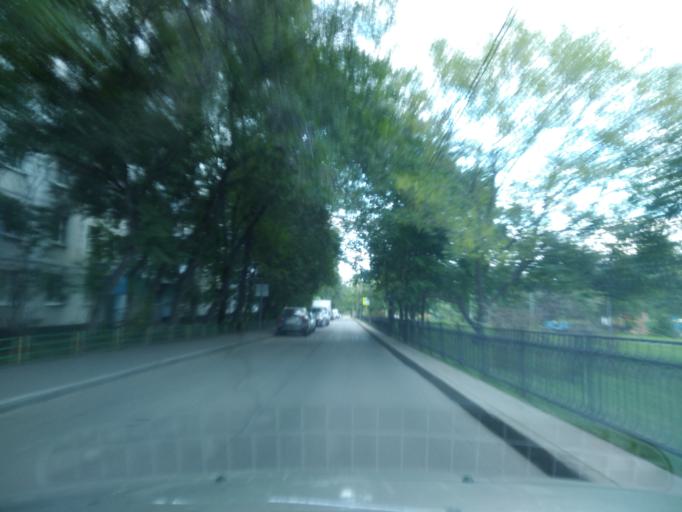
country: RU
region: Moscow
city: Strogino
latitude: 55.8155
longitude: 37.4006
